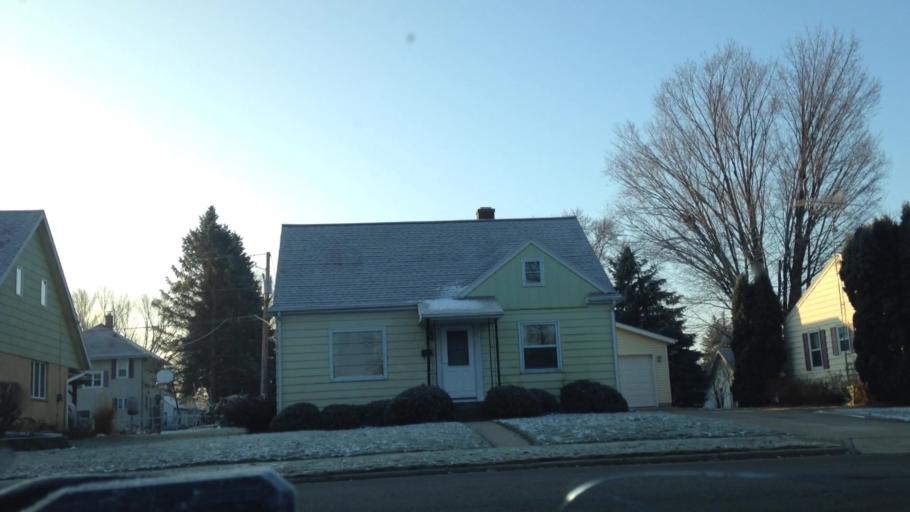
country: US
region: Wisconsin
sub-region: Dodge County
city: Mayville
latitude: 43.4977
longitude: -88.5550
